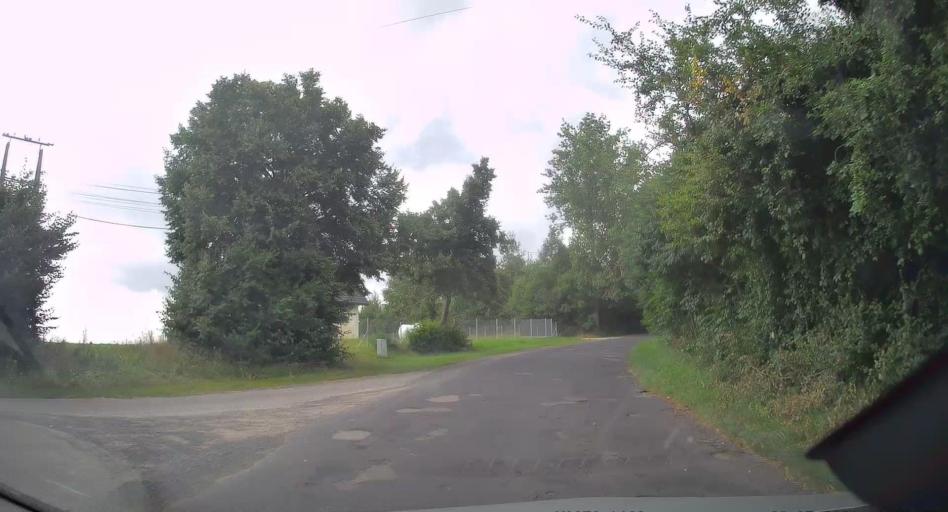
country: PL
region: Lodz Voivodeship
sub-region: Powiat rawski
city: Rawa Mazowiecka
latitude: 51.7713
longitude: 20.1821
